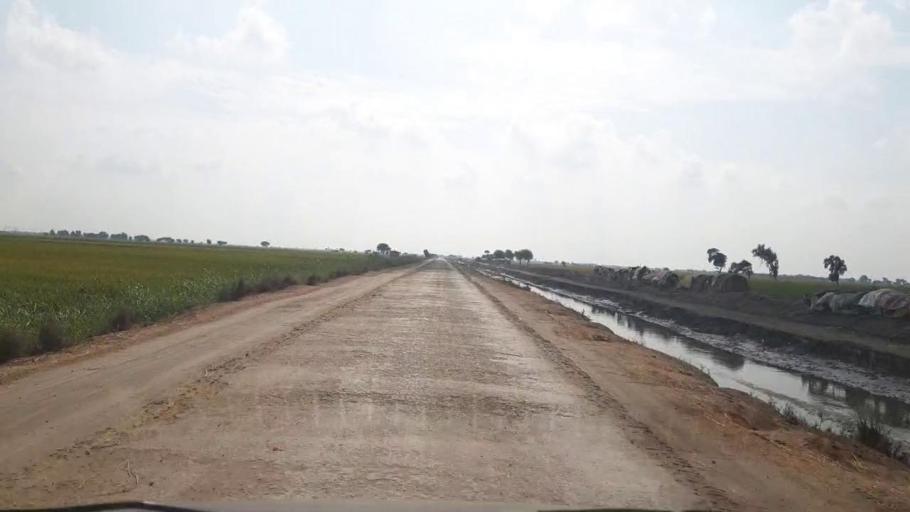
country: PK
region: Sindh
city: Kario
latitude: 24.5879
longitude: 68.5746
